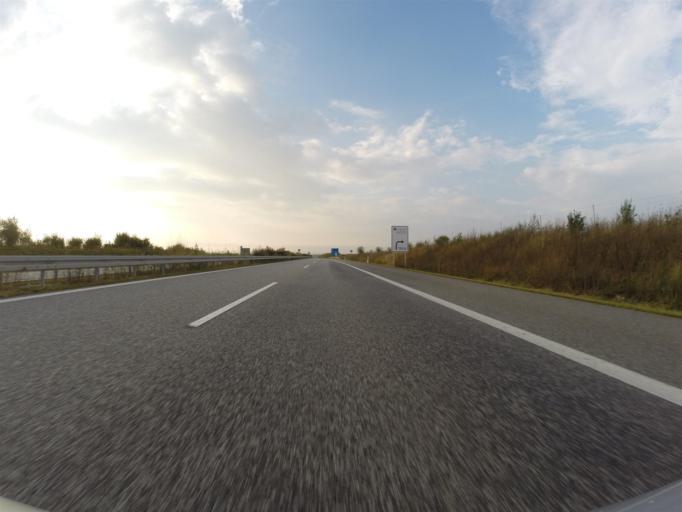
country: DE
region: Saxony-Anhalt
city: Zscherben
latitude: 51.4743
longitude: 11.8517
